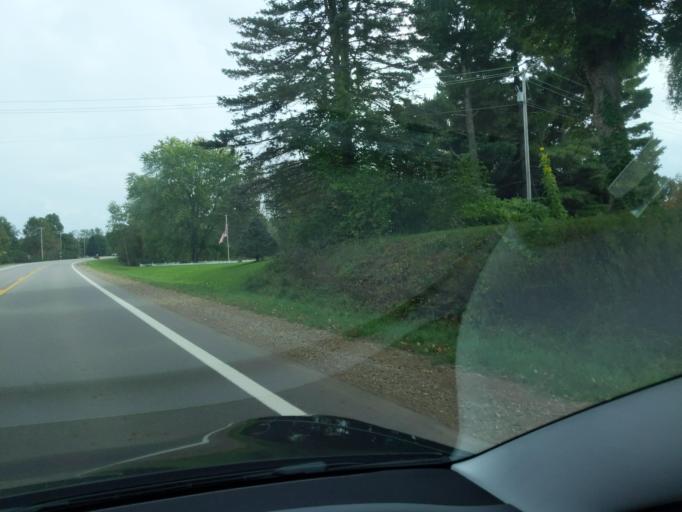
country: US
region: Michigan
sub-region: Eaton County
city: Eaton Rapids
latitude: 42.5252
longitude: -84.6972
